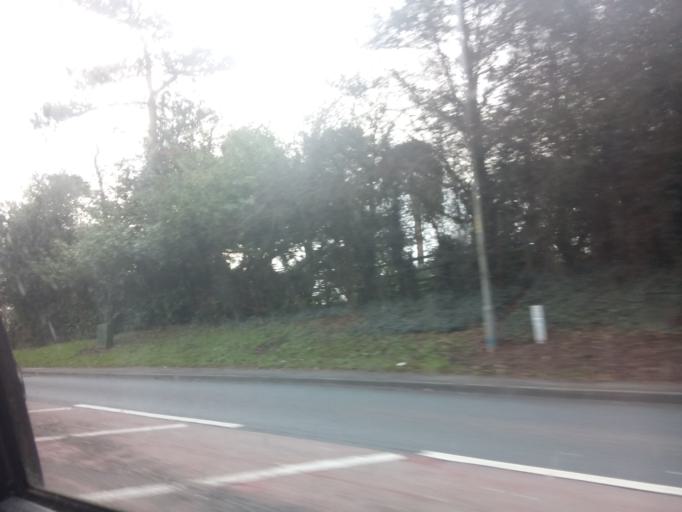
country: GB
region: England
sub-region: Worcestershire
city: Bromsgrove
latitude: 52.3582
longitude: -2.0462
